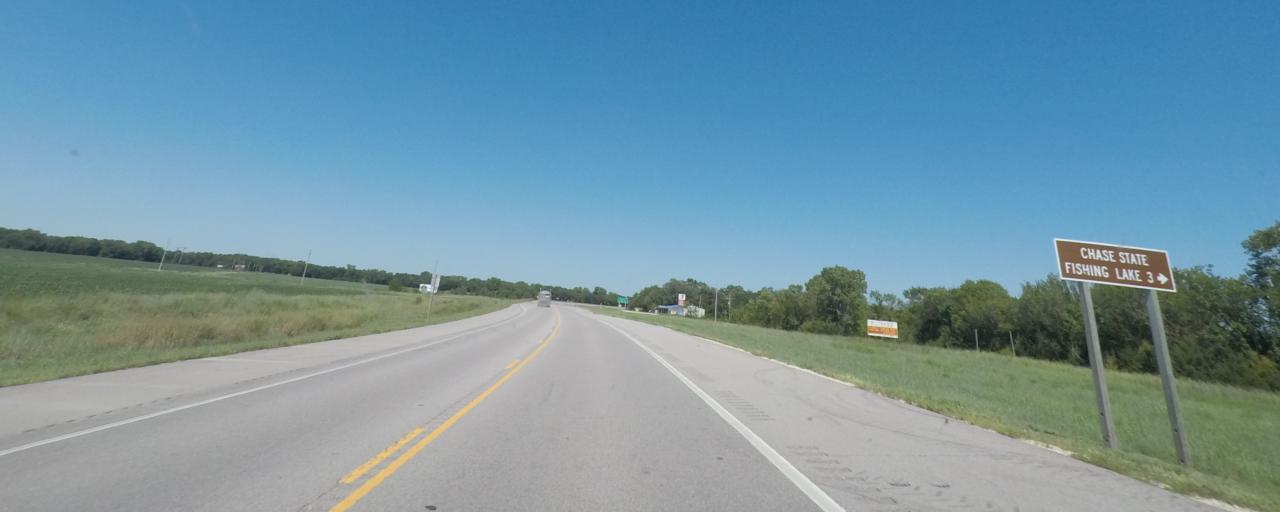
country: US
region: Kansas
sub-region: Chase County
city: Cottonwood Falls
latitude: 38.3713
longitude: -96.6513
